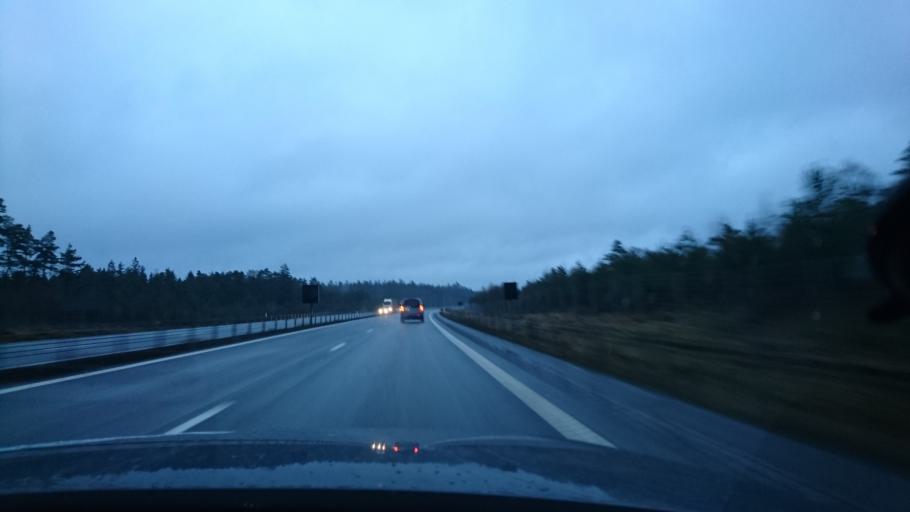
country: SE
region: Kronoberg
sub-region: Markaryds Kommun
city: Markaryd
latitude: 56.3839
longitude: 13.5077
